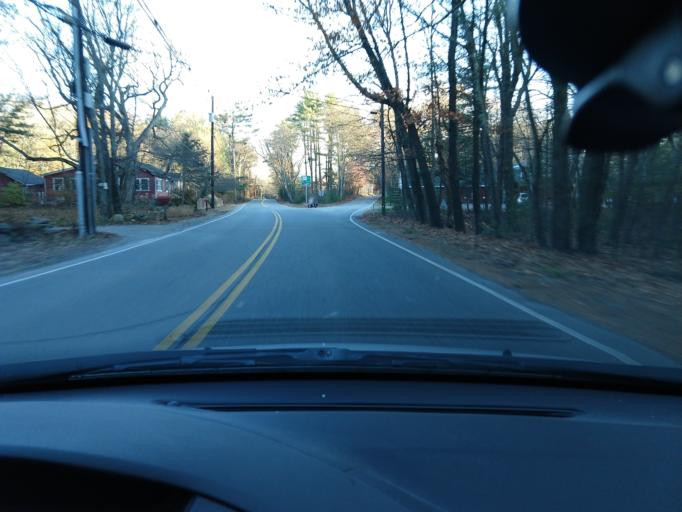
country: US
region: Massachusetts
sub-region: Middlesex County
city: Carlisle
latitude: 42.5164
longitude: -71.3242
